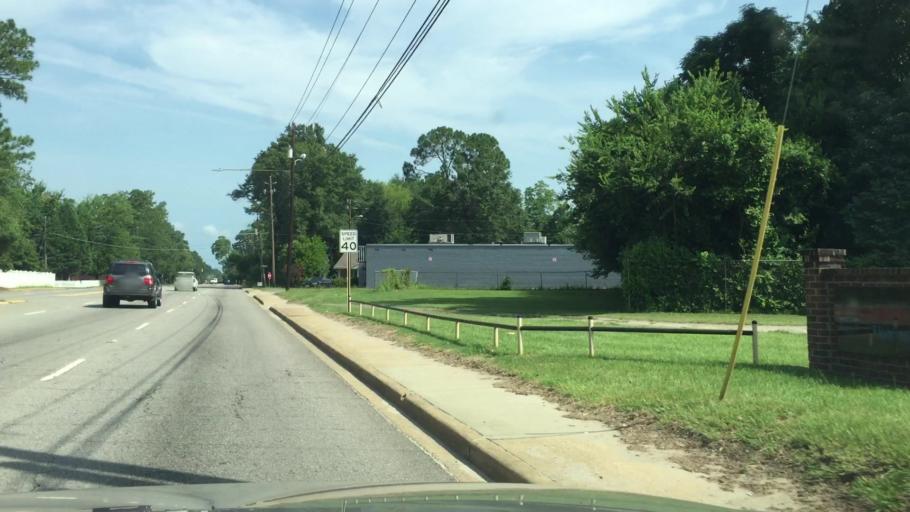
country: US
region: South Carolina
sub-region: Sumter County
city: Sumter
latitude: 33.9210
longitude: -80.3605
